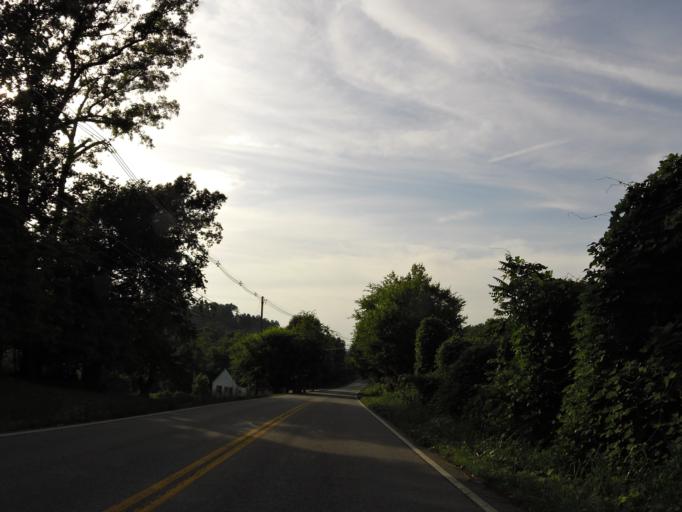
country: US
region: Tennessee
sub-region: Blount County
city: Louisville
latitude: 35.8005
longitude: -84.0194
